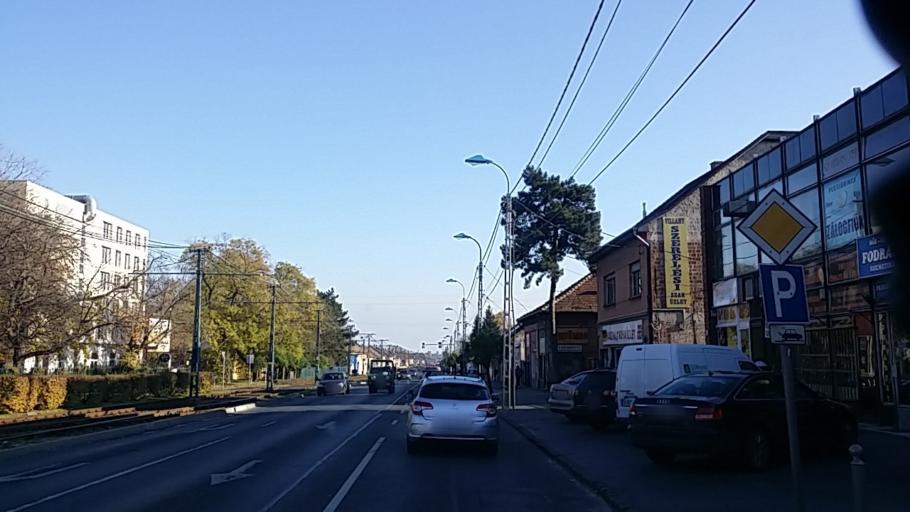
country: HU
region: Budapest
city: Budapest XVIII. keruelet
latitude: 47.4398
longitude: 19.1866
